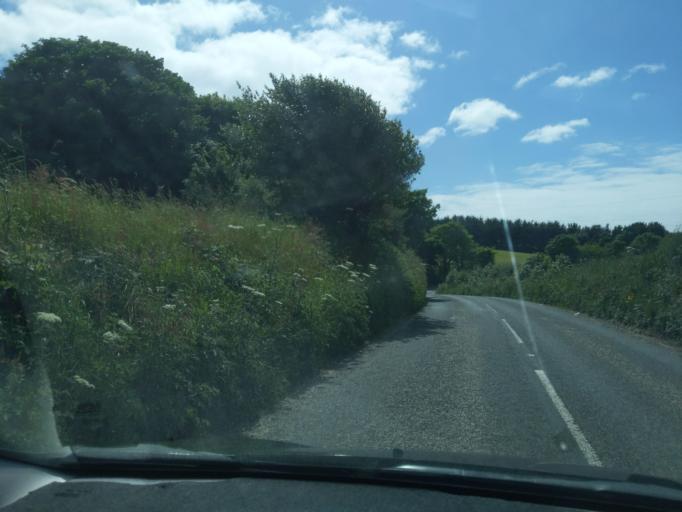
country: GB
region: England
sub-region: Cornwall
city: Perranporth
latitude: 50.2974
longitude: -5.1380
